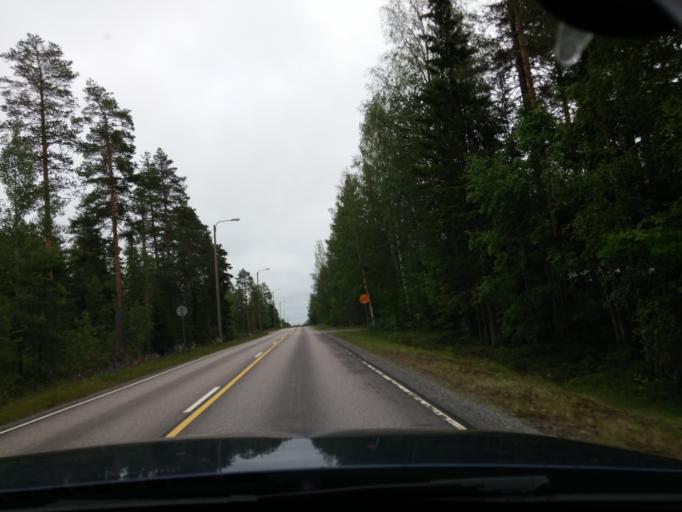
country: FI
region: Central Finland
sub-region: Saarijaervi-Viitasaari
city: Pylkoenmaeki
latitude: 62.6176
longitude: 24.7510
